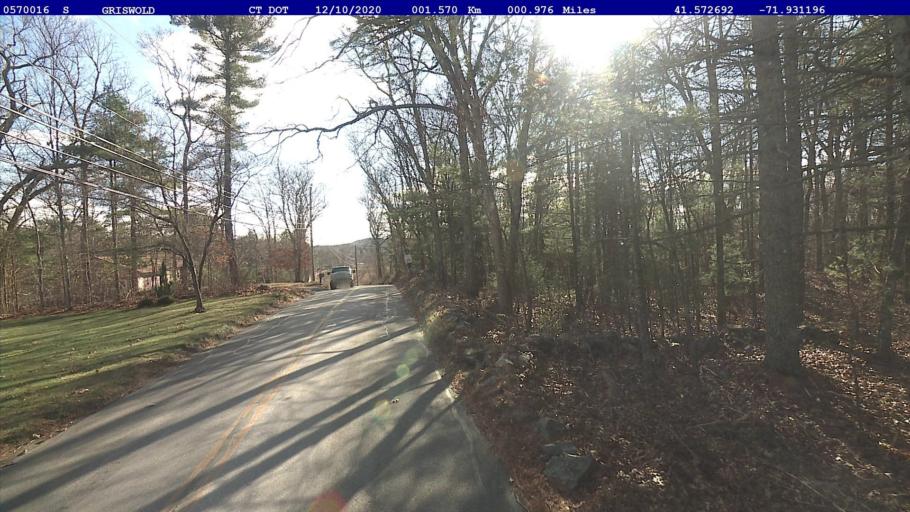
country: US
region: Connecticut
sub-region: New London County
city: Jewett City
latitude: 41.5727
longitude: -71.9312
